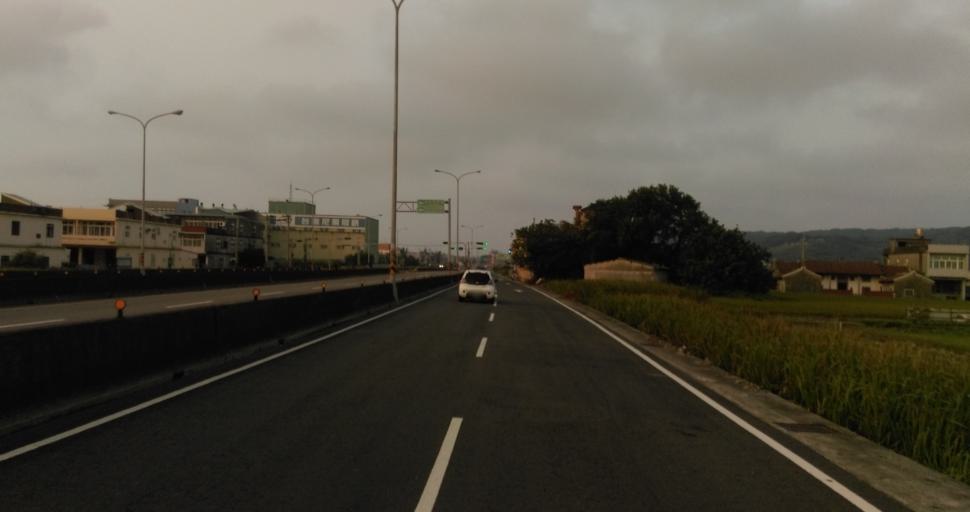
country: TW
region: Taiwan
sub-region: Hsinchu
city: Zhubei
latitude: 24.8670
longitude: 120.9534
